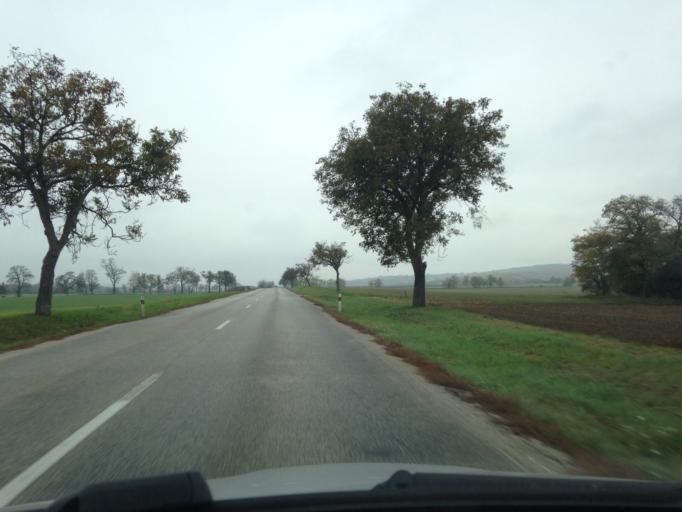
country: HU
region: Komarom-Esztergom
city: Nyergesujfalu
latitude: 47.8278
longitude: 18.5562
